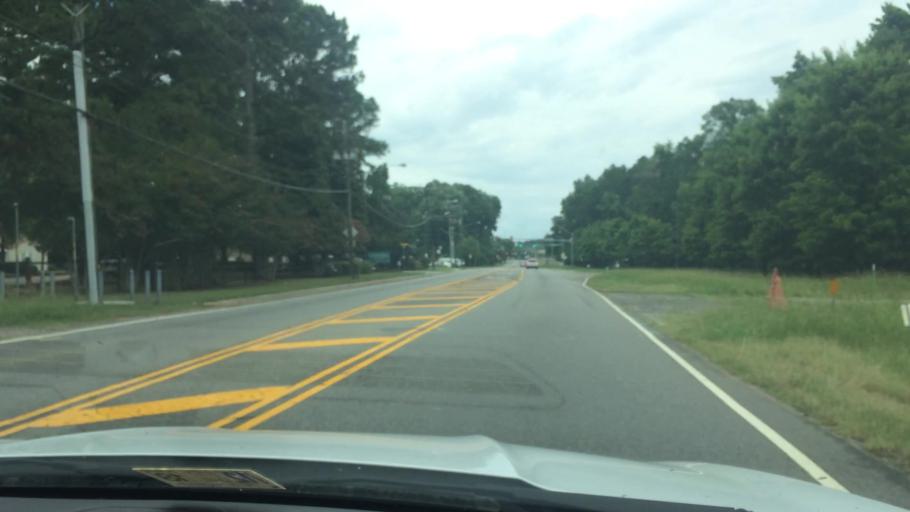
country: US
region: Virginia
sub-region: York County
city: Yorktown
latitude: 37.1843
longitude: -76.5719
